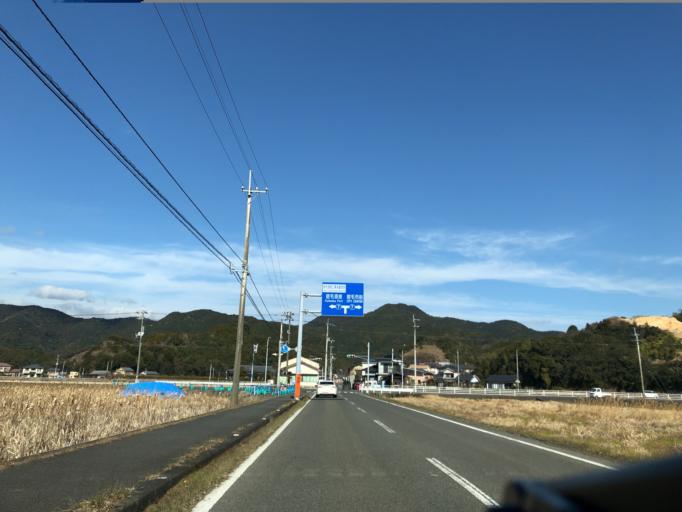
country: JP
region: Kochi
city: Sukumo
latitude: 32.9295
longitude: 132.6963
